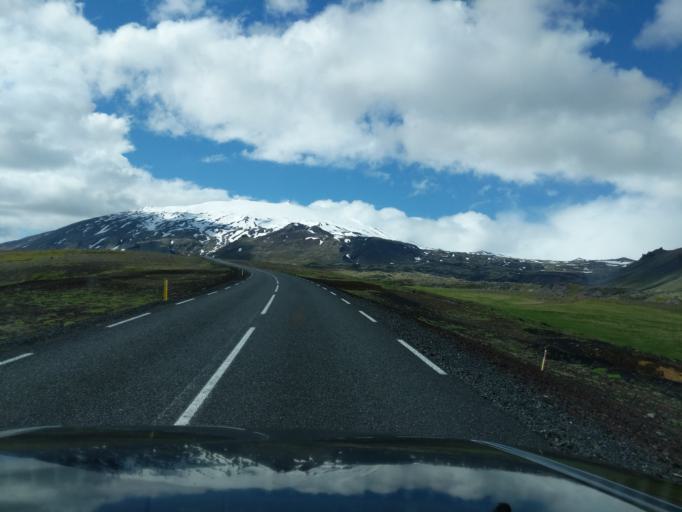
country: IS
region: West
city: Olafsvik
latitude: 64.7519
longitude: -23.6602
